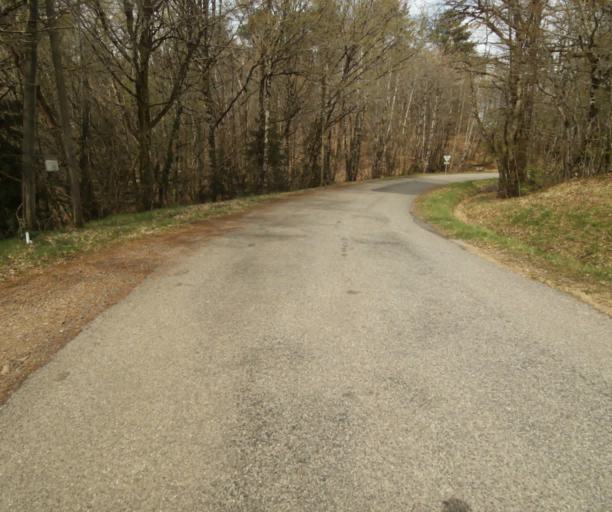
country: FR
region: Limousin
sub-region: Departement de la Correze
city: Laguenne
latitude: 45.2096
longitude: 1.8636
